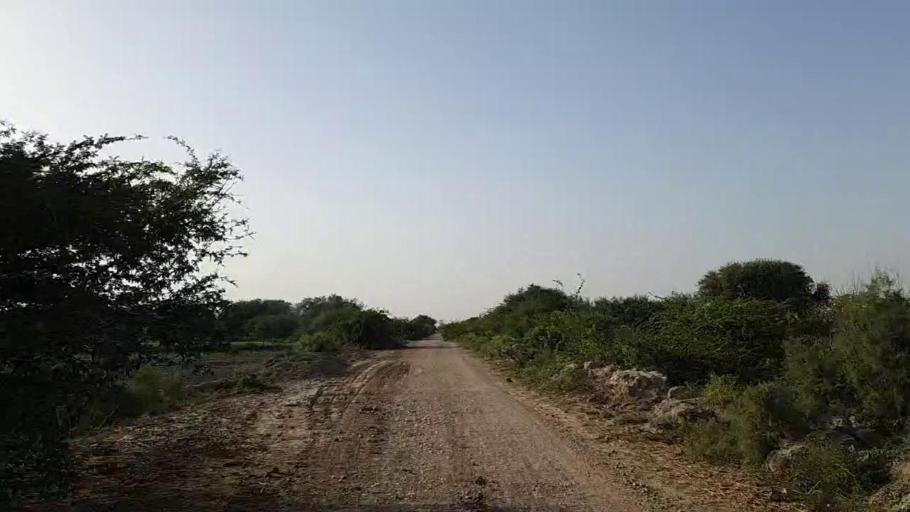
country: PK
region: Sindh
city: Jati
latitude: 24.3393
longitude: 68.1497
